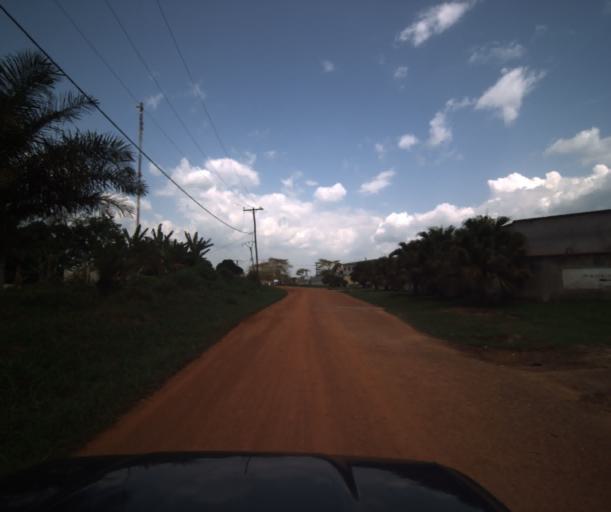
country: CM
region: Centre
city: Eseka
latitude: 3.5466
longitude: 11.0311
